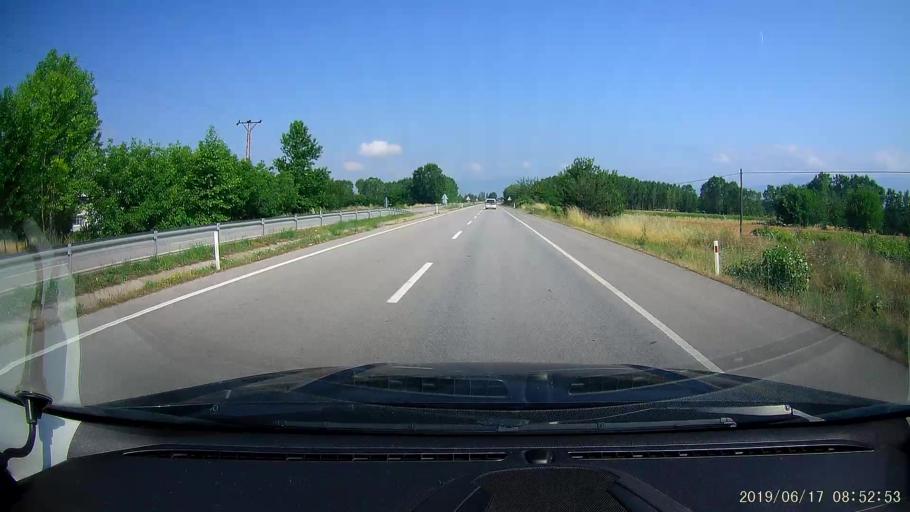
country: TR
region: Tokat
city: Erbaa
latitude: 40.7035
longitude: 36.4897
